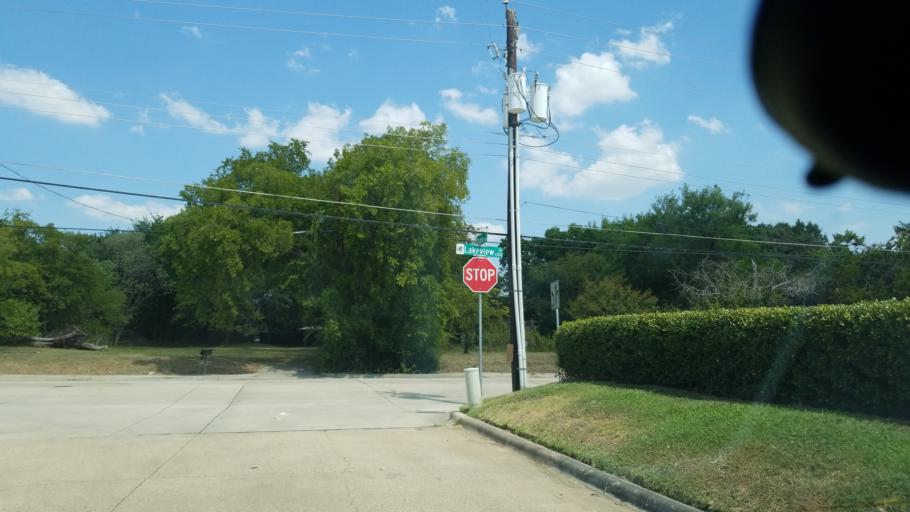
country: US
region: Texas
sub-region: Dallas County
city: Grand Prairie
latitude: 32.7102
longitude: -96.9868
